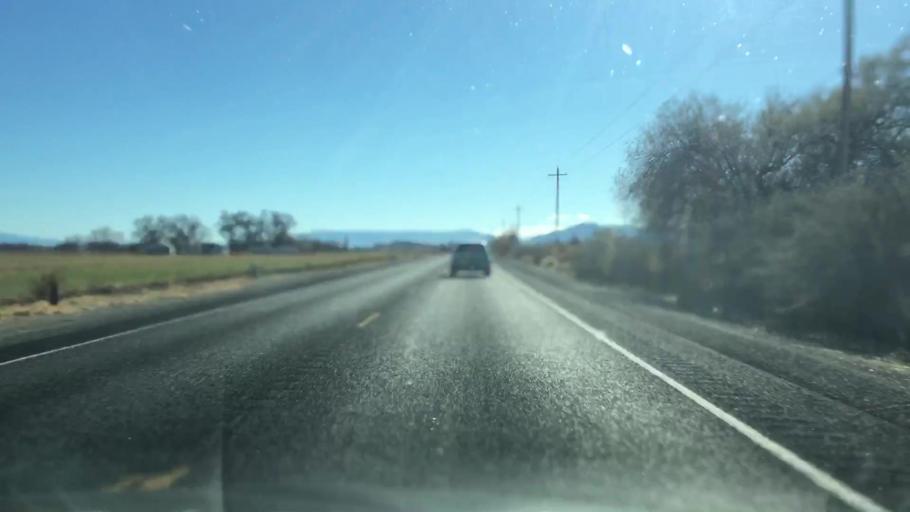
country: US
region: Nevada
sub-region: Lyon County
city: Yerington
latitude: 39.0657
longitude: -119.1813
